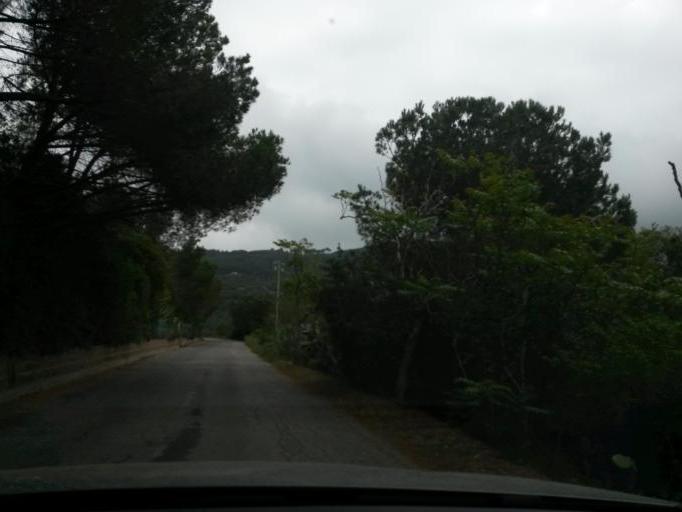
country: IT
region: Tuscany
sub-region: Provincia di Livorno
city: Capoliveri
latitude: 42.7350
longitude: 10.3730
